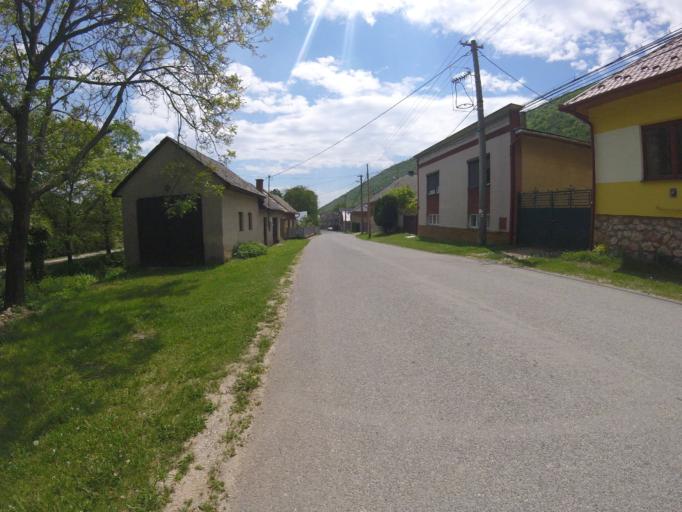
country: SK
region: Kosicky
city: Medzev
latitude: 48.6307
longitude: 20.8511
